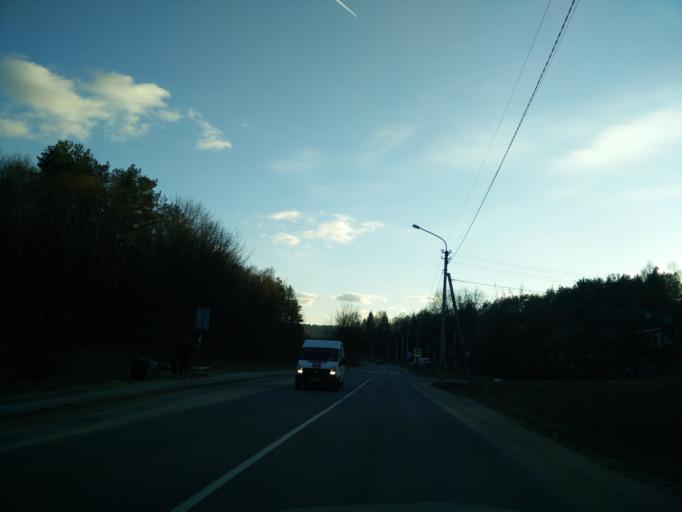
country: LT
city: Skaidiskes
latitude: 54.6996
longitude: 25.4022
